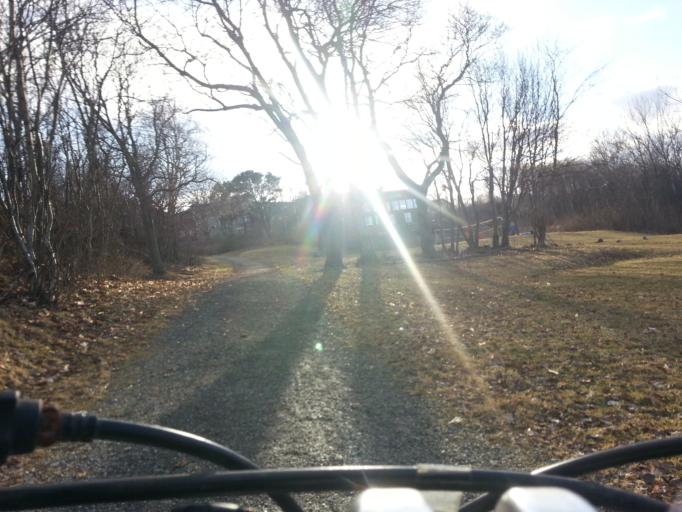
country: NO
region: Sor-Trondelag
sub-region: Trondheim
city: Trondheim
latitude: 63.4564
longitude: 10.4516
